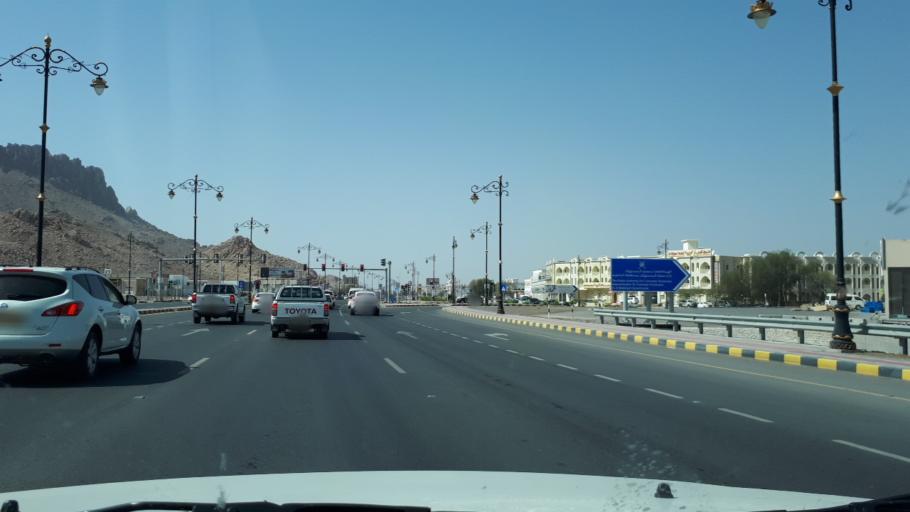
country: OM
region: Muhafazat ad Dakhiliyah
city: Nizwa
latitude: 22.9076
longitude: 57.5342
